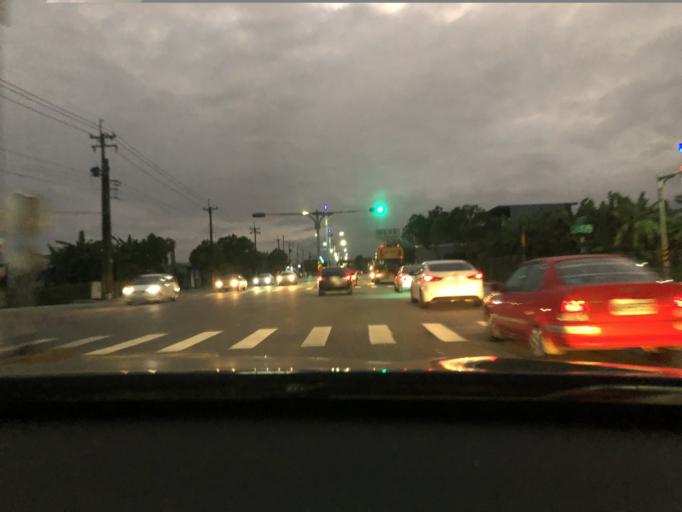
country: TW
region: Taiwan
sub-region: Hualien
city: Hualian
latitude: 23.9650
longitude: 121.5671
